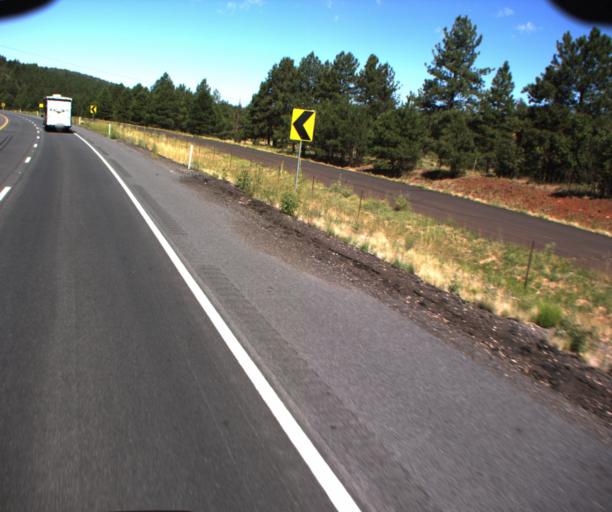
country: US
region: Arizona
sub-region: Coconino County
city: Williams
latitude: 35.2219
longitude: -112.2927
